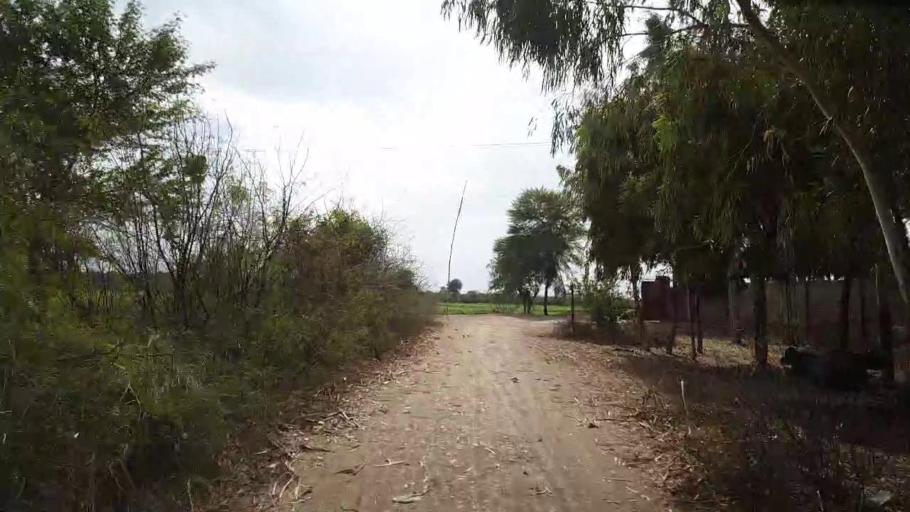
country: PK
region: Sindh
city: Tando Jam
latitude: 25.5428
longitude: 68.5715
